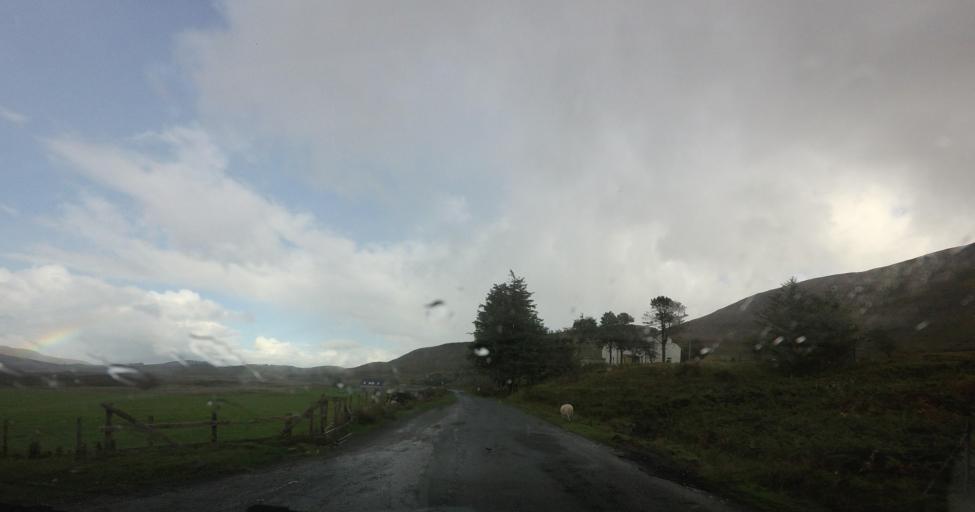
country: GB
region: Scotland
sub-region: Highland
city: Portree
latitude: 57.2177
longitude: -5.9408
